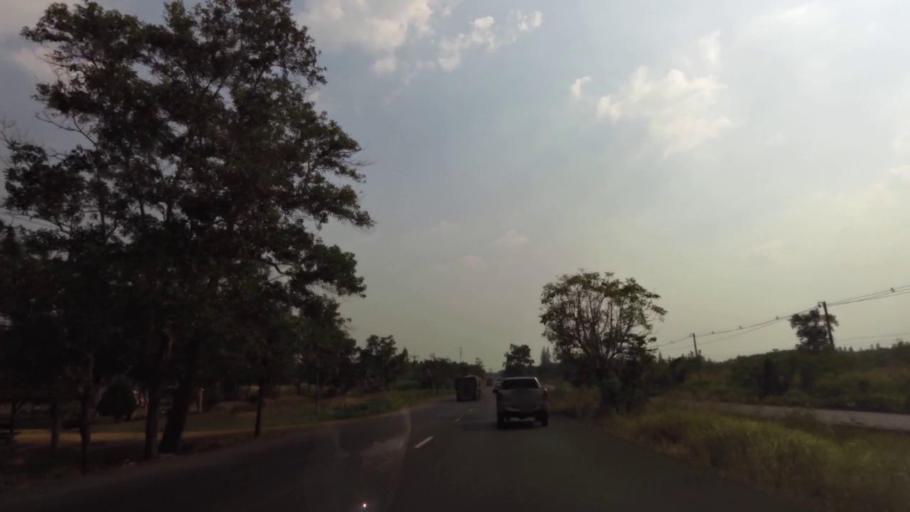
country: TH
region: Rayong
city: Wang Chan
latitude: 12.9798
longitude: 101.4917
